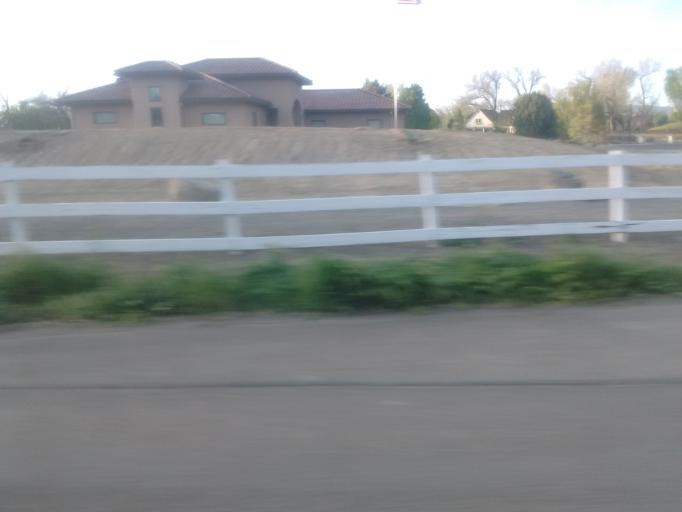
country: US
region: Colorado
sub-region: Mesa County
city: Grand Junction
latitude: 39.1064
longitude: -108.5776
